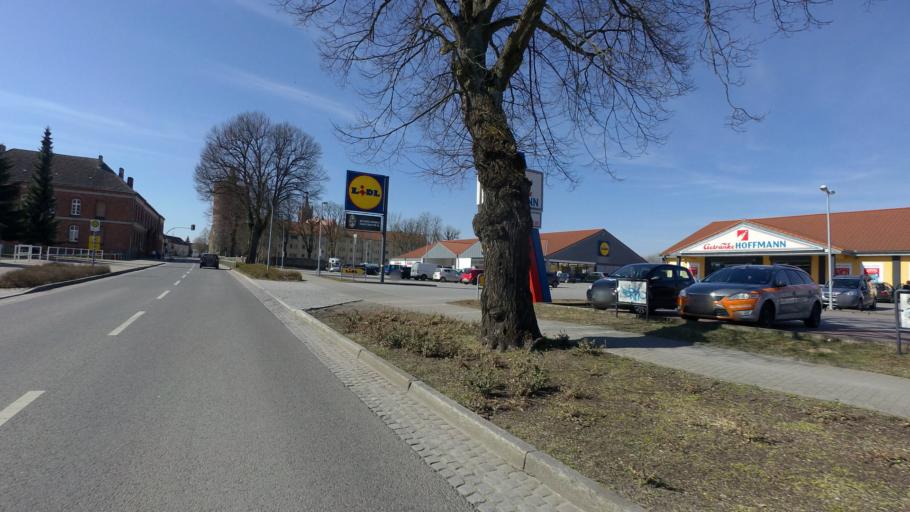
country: DE
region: Brandenburg
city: Muncheberg
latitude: 52.5014
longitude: 14.1469
